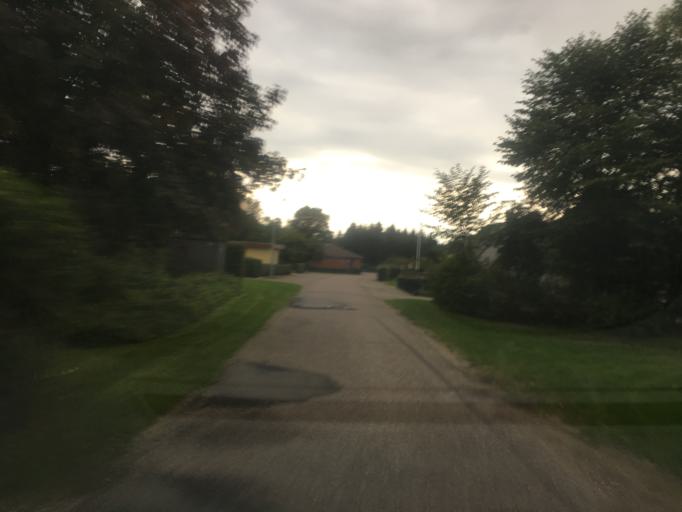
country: DE
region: Schleswig-Holstein
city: Ellhoft
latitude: 54.9318
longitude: 8.9232
